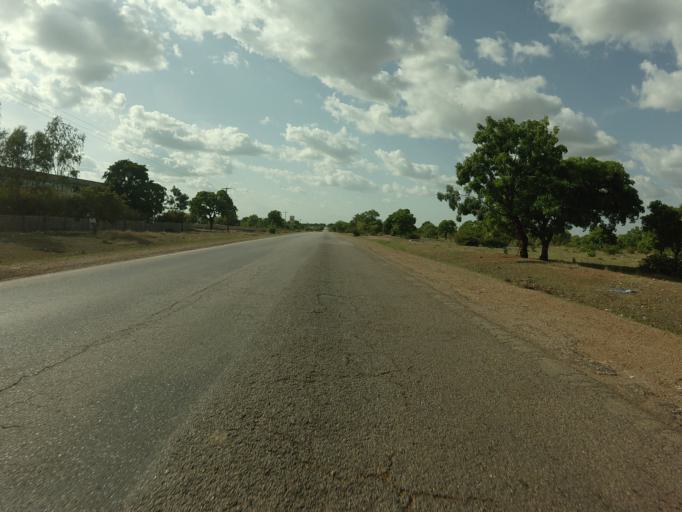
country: GH
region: Upper East
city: Bolgatanga
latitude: 10.6502
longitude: -0.8578
